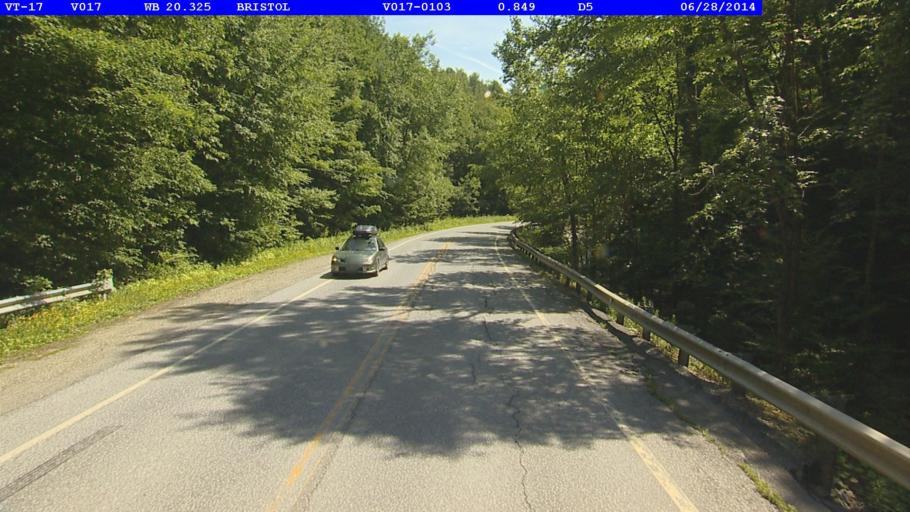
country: US
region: Vermont
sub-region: Addison County
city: Bristol
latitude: 44.1557
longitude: -73.0423
